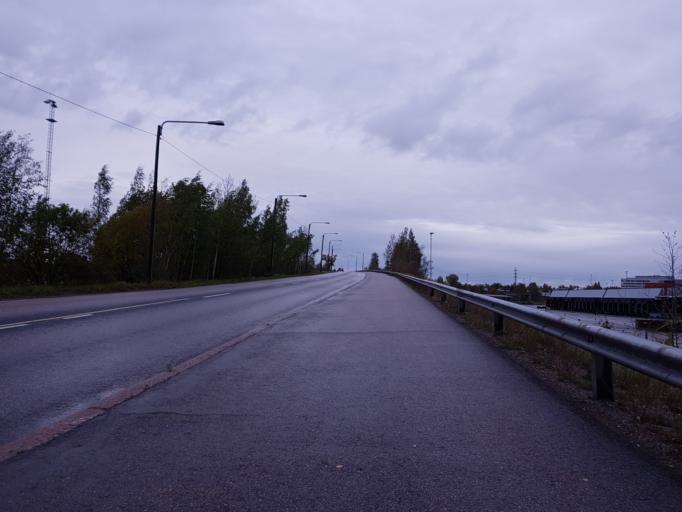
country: FI
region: Uusimaa
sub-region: Helsinki
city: Helsinki
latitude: 60.2145
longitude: 24.9330
